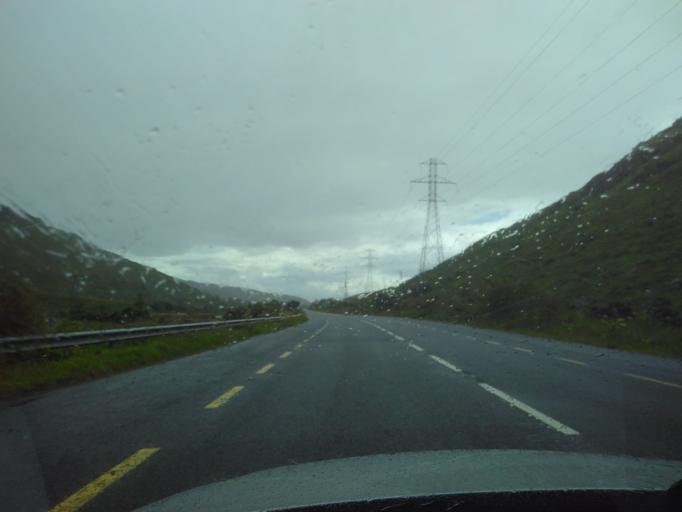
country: IE
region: Ulster
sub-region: County Donegal
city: Donegal
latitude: 54.7174
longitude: -7.9587
